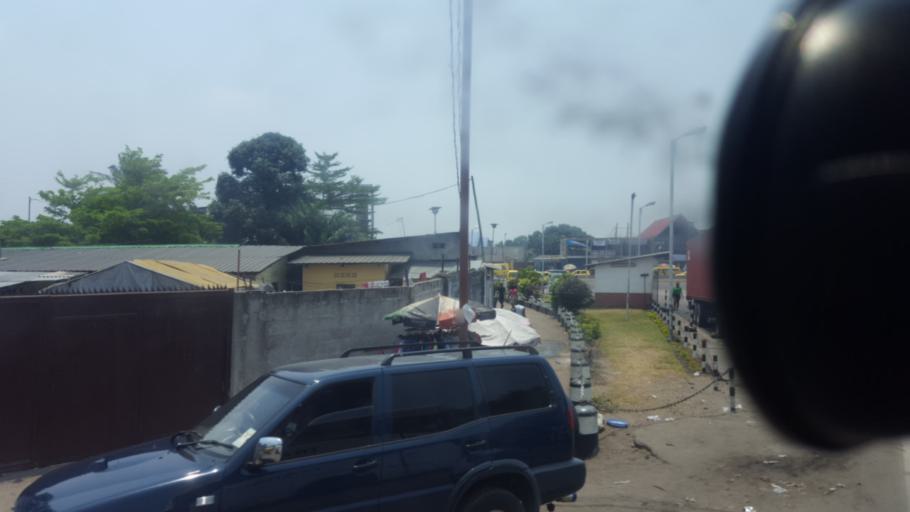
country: CD
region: Kinshasa
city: Masina
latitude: -4.3848
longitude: 15.3575
